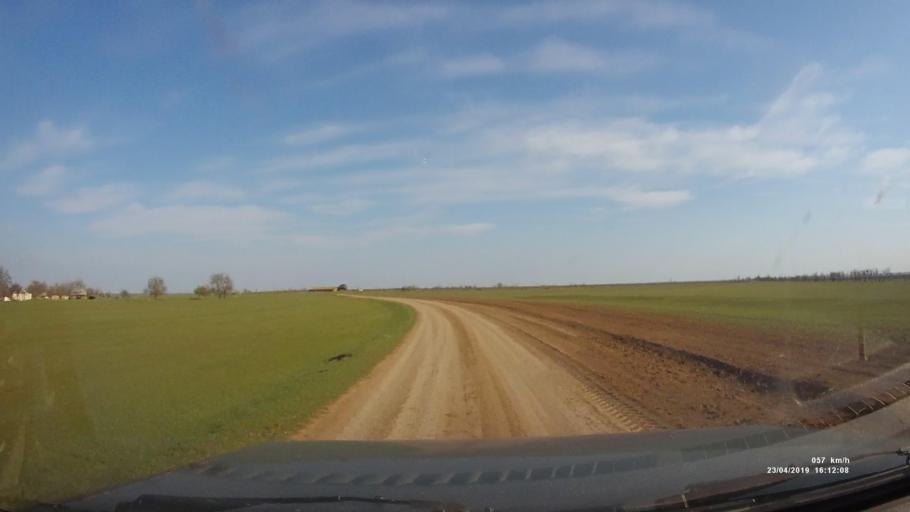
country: RU
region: Kalmykiya
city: Priyutnoye
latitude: 46.4682
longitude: 43.1235
